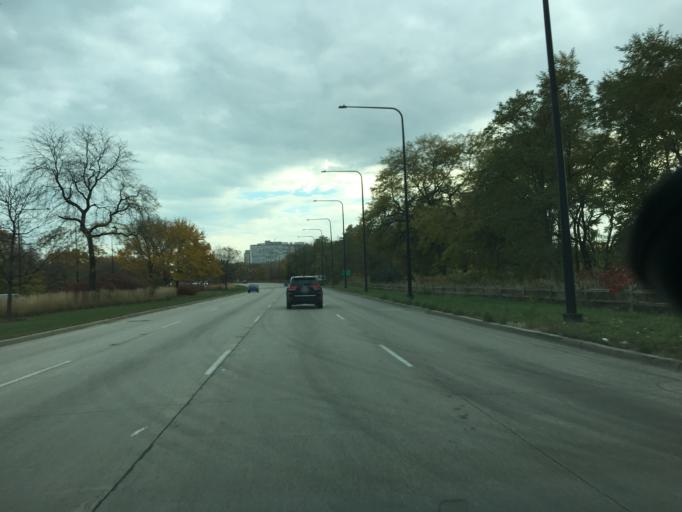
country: US
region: Illinois
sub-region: Cook County
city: Chicago
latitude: 41.8166
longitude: -87.5950
